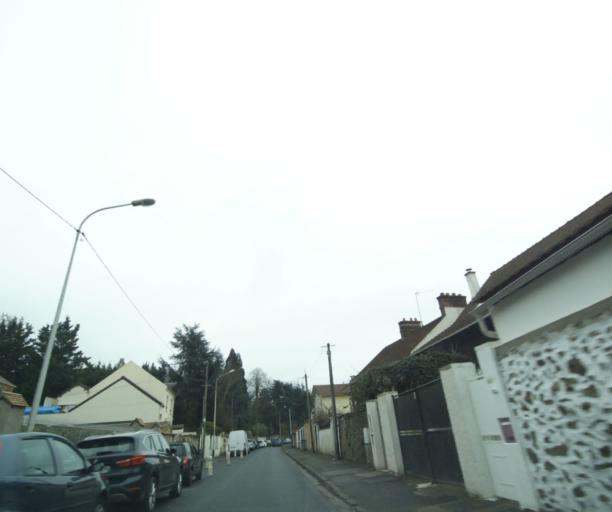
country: FR
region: Ile-de-France
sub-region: Departement de l'Essonne
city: Champlan
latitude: 48.7086
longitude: 2.2706
